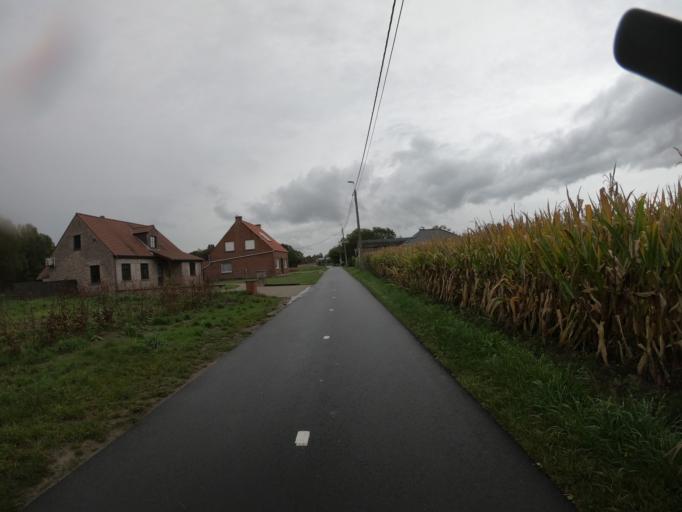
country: BE
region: Flanders
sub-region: Provincie Vlaams-Brabant
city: Rotselaar
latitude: 50.9491
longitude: 4.7302
